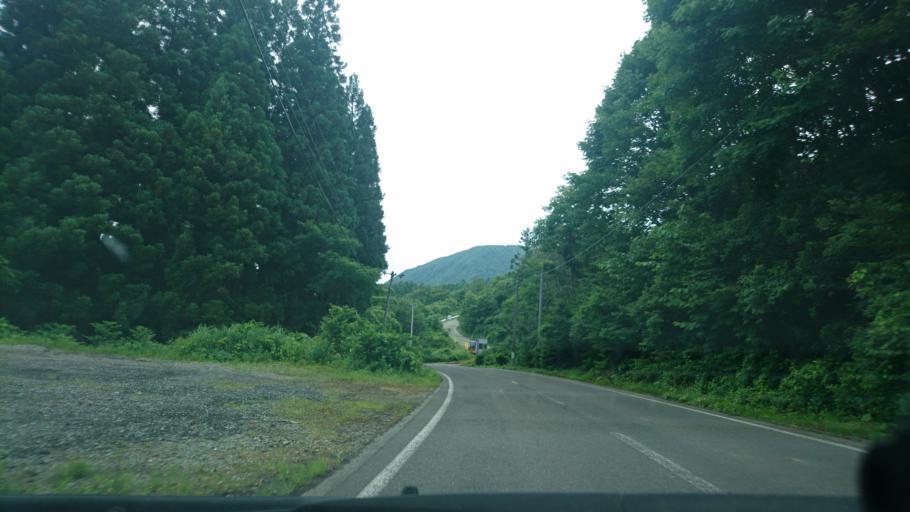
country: JP
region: Akita
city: Yokotemachi
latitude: 39.1731
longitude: 140.7326
